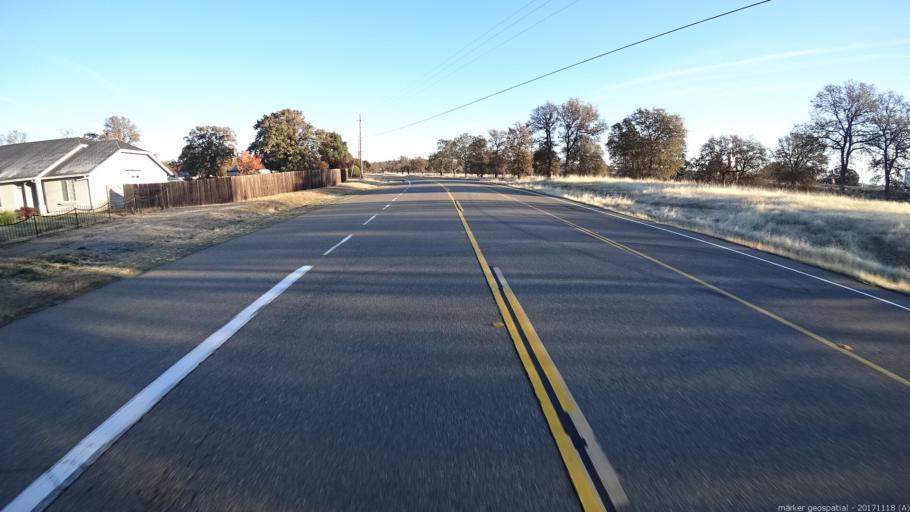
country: US
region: California
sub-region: Shasta County
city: Cottonwood
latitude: 40.4016
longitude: -122.2835
